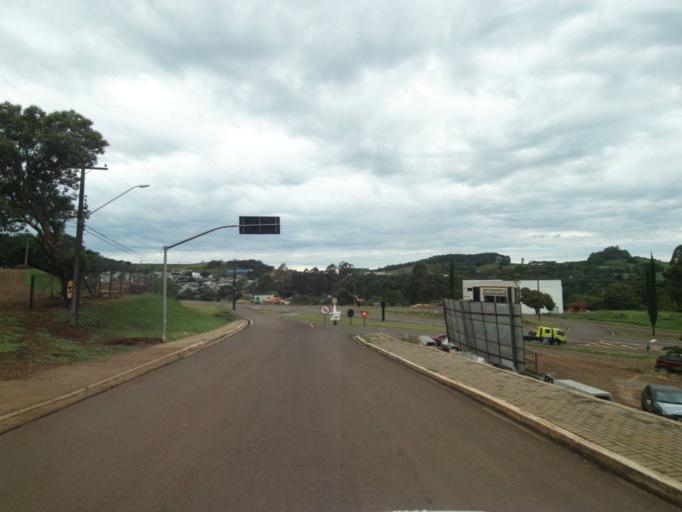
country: BR
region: Parana
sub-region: Guaraniacu
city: Guaraniacu
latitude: -25.1083
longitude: -52.8561
